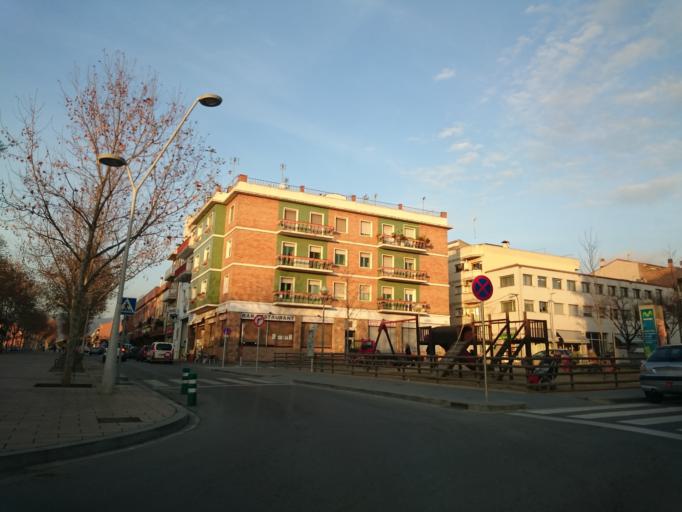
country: ES
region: Catalonia
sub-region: Provincia de Barcelona
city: Les Franqueses del Valles
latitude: 41.6324
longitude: 2.2962
